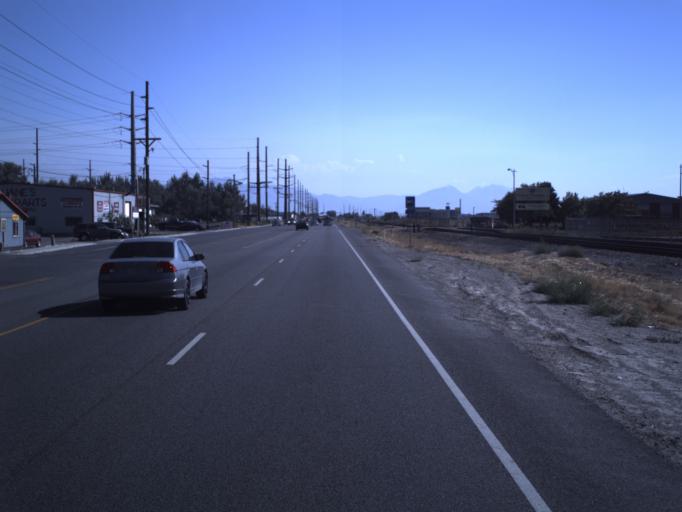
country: US
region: Utah
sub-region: Utah County
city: Lindon
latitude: 40.3194
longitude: -111.7361
